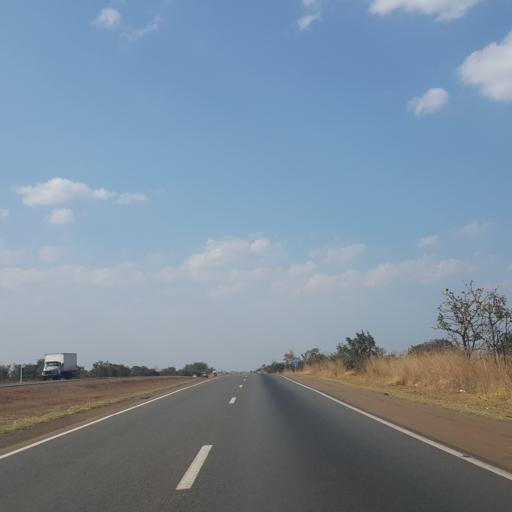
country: BR
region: Goias
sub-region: Abadiania
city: Abadiania
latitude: -16.1998
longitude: -48.7353
